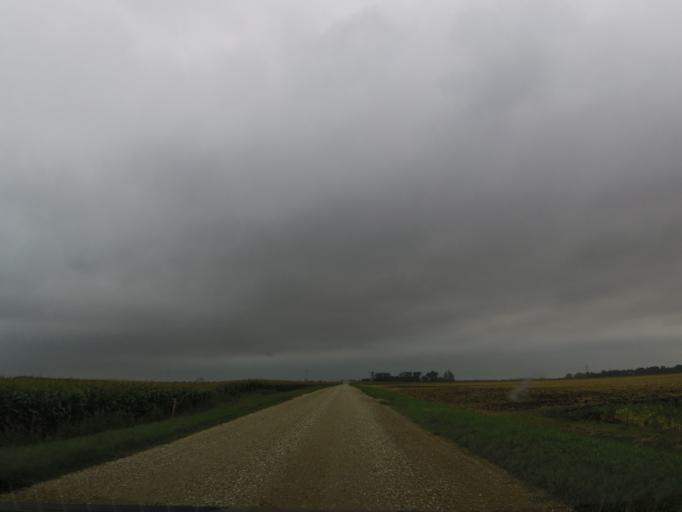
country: US
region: North Dakota
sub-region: Walsh County
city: Grafton
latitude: 48.4705
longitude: -97.1793
